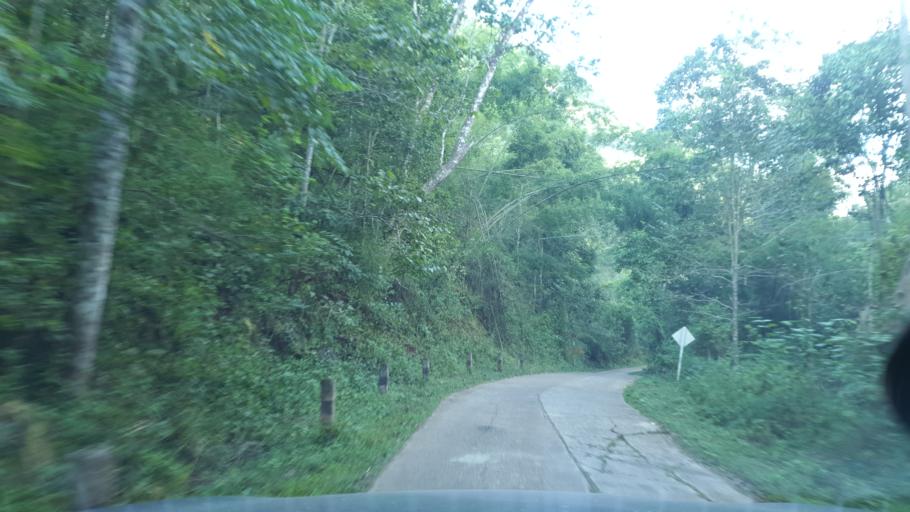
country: TH
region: Chiang Mai
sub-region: Amphoe Chiang Dao
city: Chiang Dao
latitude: 19.3896
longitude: 98.7691
